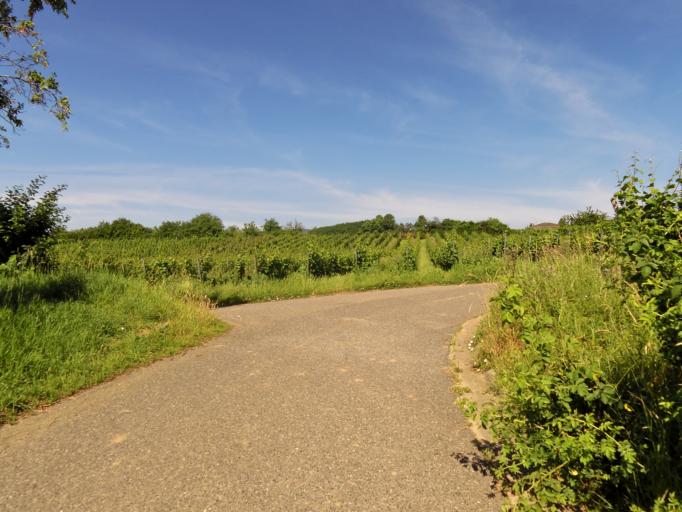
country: DE
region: Rheinland-Pfalz
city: Edenkoben
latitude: 49.2748
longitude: 8.1243
